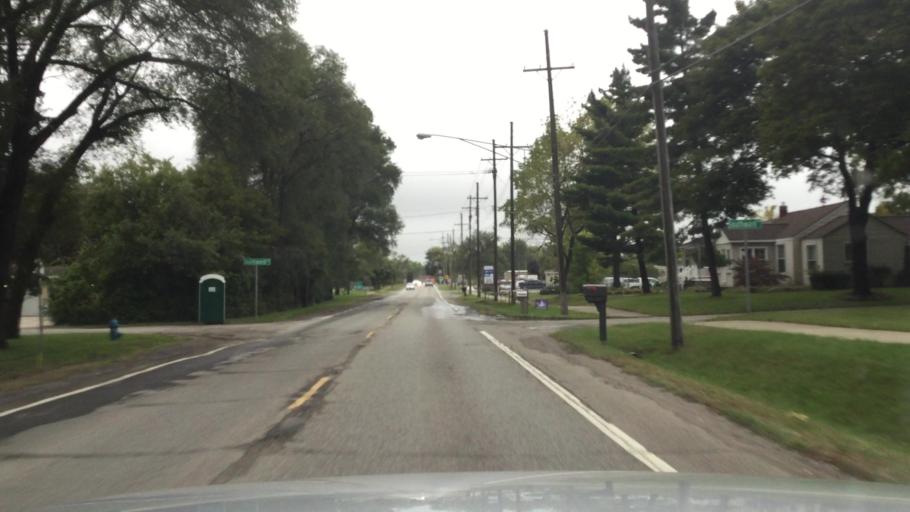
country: US
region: Michigan
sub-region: Oakland County
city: Waterford
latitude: 42.6971
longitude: -83.4077
